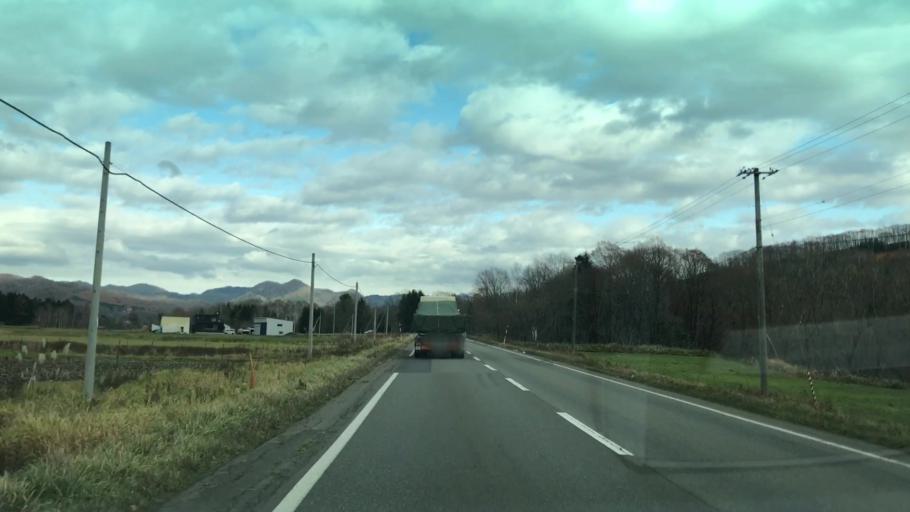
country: JP
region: Hokkaido
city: Shimo-furano
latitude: 42.8606
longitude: 142.4201
